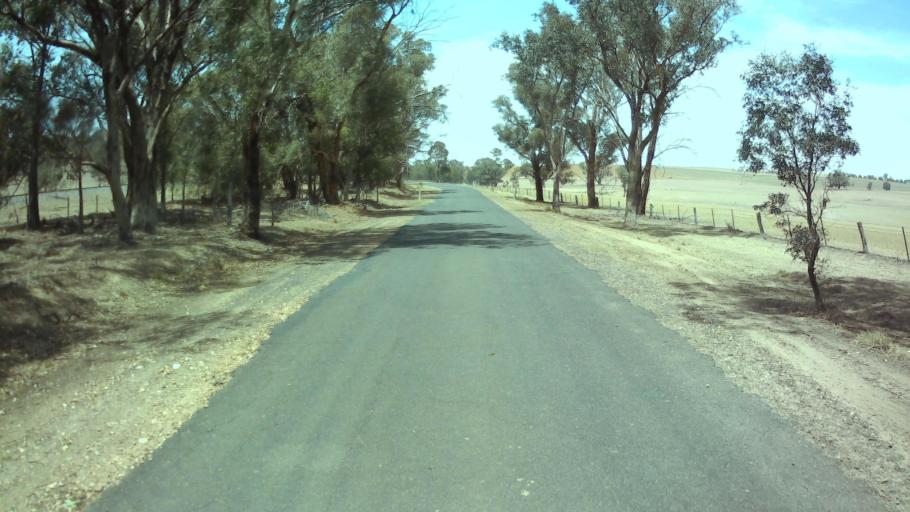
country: AU
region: New South Wales
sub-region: Weddin
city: Grenfell
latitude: -34.0215
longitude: 148.4326
